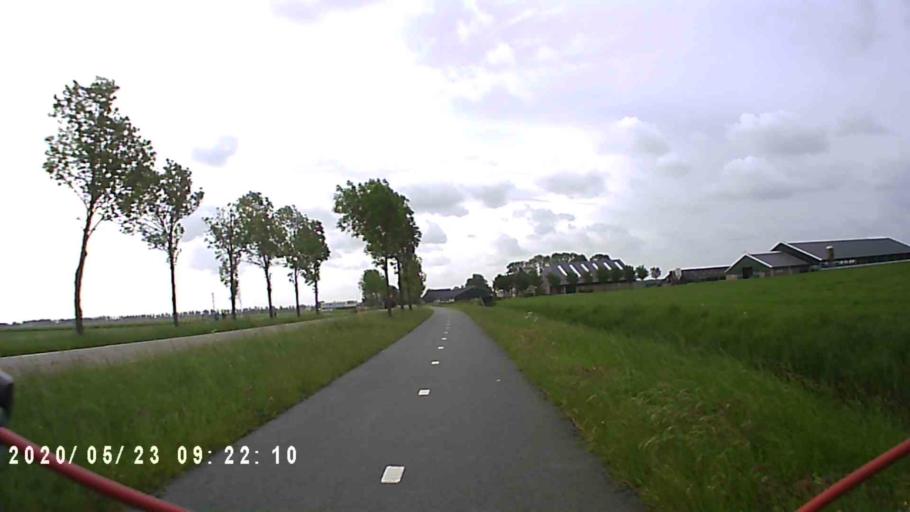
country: NL
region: Groningen
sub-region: Gemeente Bedum
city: Bedum
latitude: 53.2909
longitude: 6.6786
